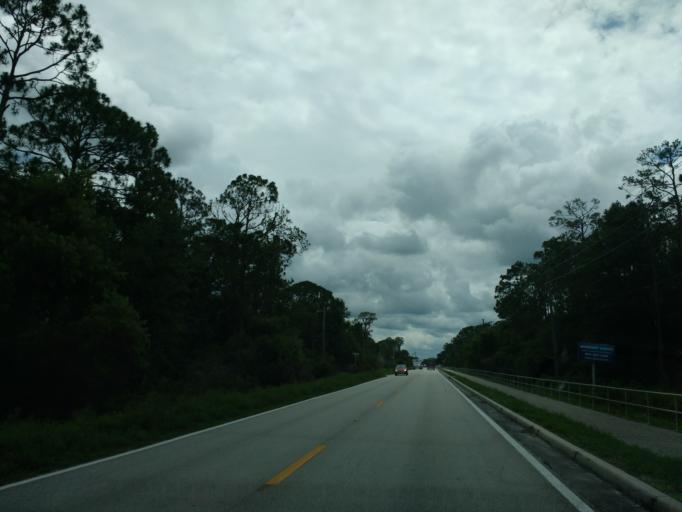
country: US
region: Florida
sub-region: Highlands County
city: Sebring
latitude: 27.4709
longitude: -81.4914
